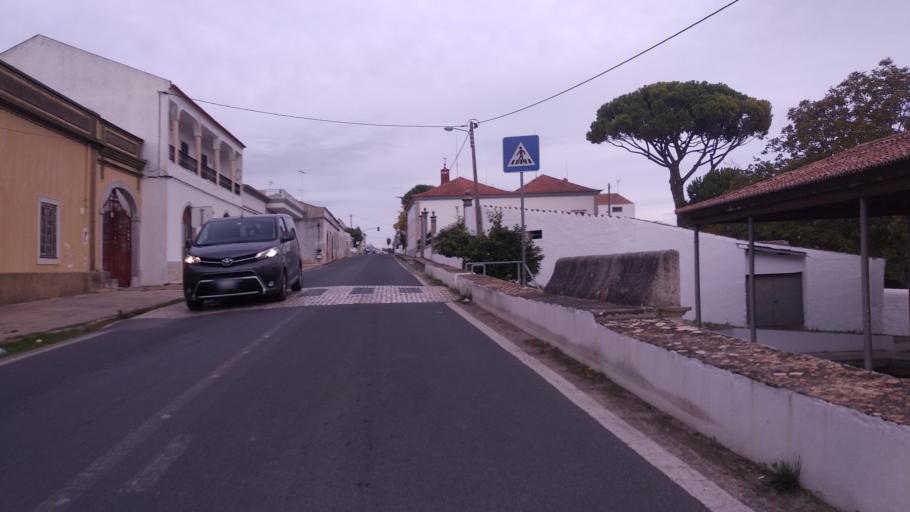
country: PT
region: Faro
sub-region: Sao Bras de Alportel
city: Sao Bras de Alportel
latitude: 37.1520
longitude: -7.9216
